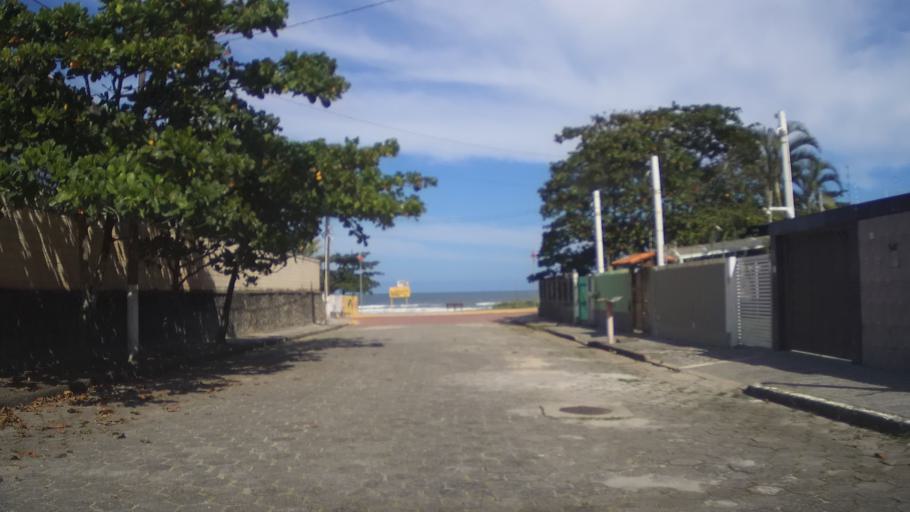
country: BR
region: Sao Paulo
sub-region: Itanhaem
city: Itanhaem
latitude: -24.1658
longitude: -46.7512
